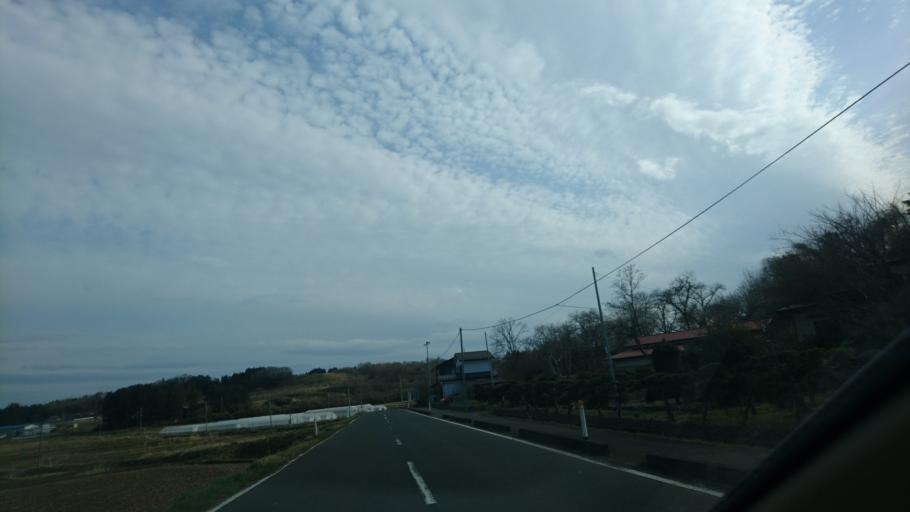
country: JP
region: Iwate
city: Ichinoseki
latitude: 38.8091
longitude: 141.0311
